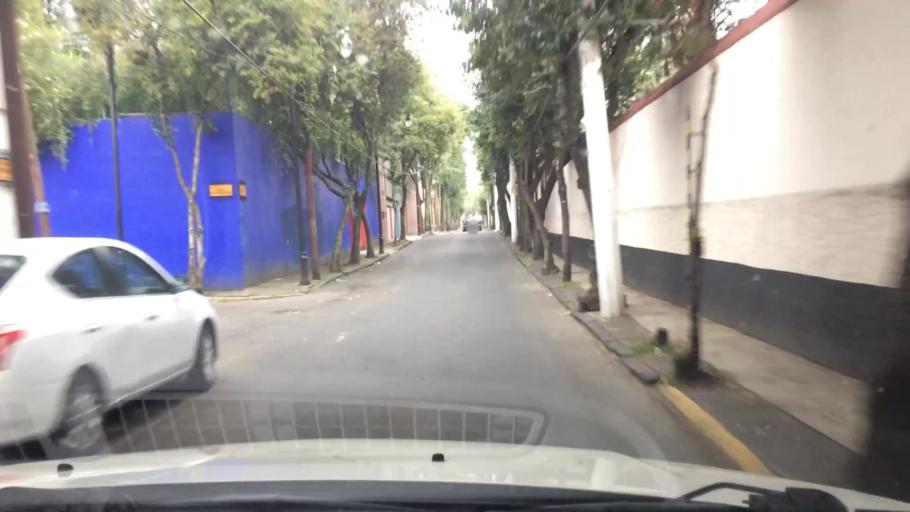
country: MX
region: Mexico City
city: Tlalpan
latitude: 19.2900
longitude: -99.1696
